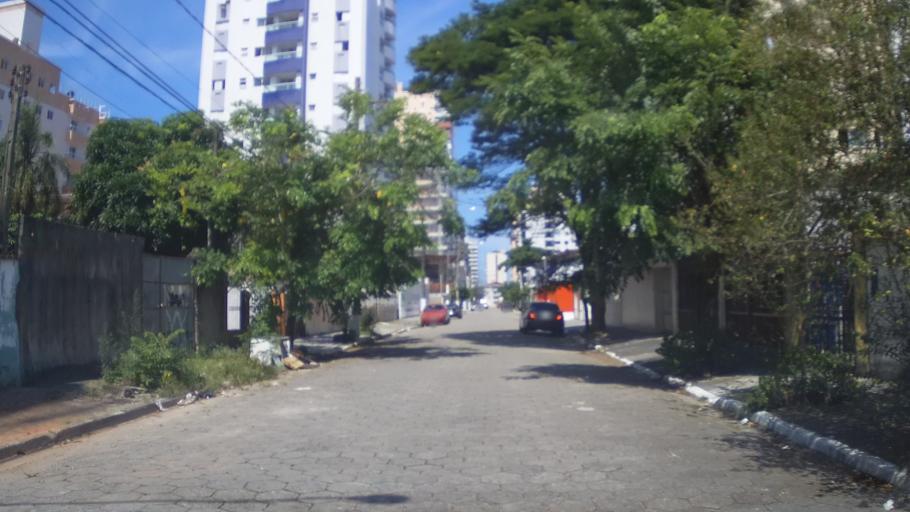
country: BR
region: Sao Paulo
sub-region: Praia Grande
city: Praia Grande
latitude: -24.0091
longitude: -46.4258
